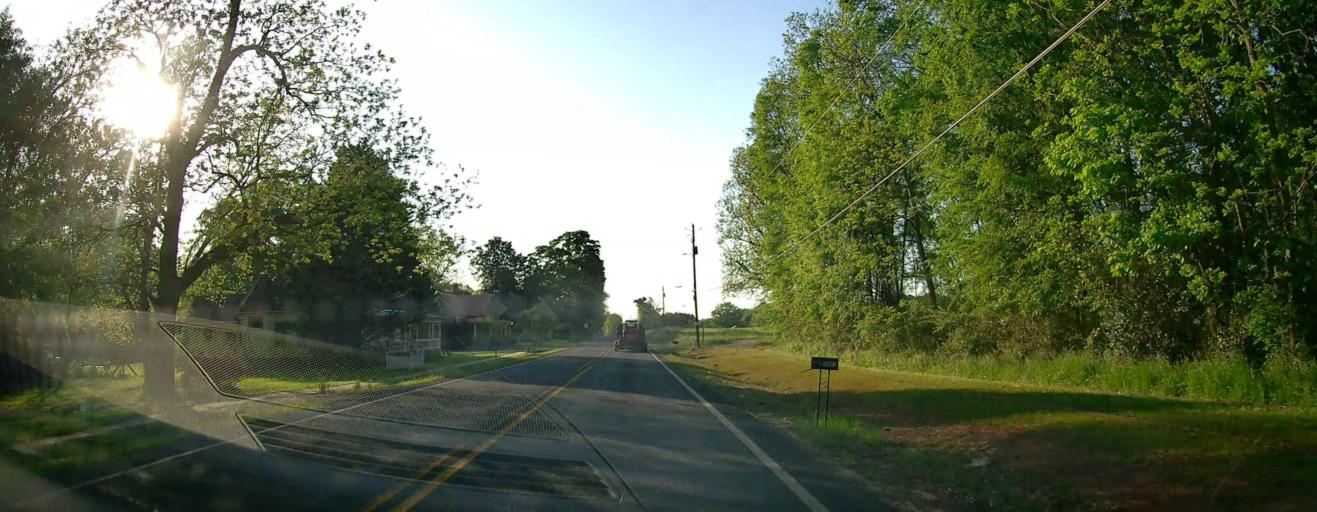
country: US
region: Georgia
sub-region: Jasper County
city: Monticello
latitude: 33.4015
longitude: -83.5912
